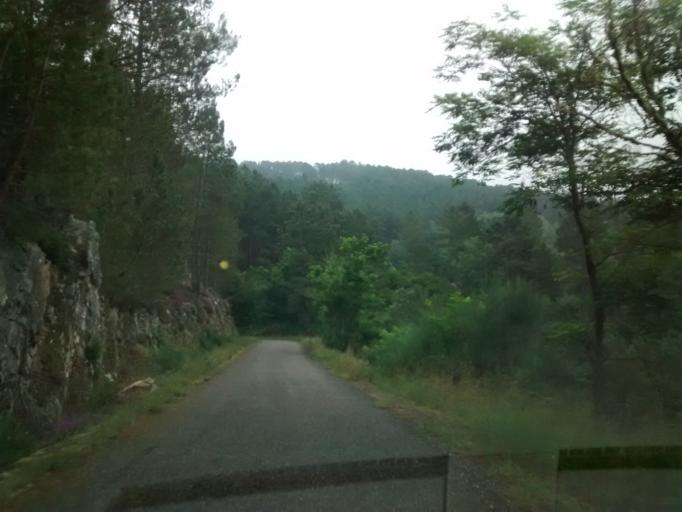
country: ES
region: Galicia
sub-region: Provincia de Ourense
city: Castro Caldelas
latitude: 42.4133
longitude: -7.3904
